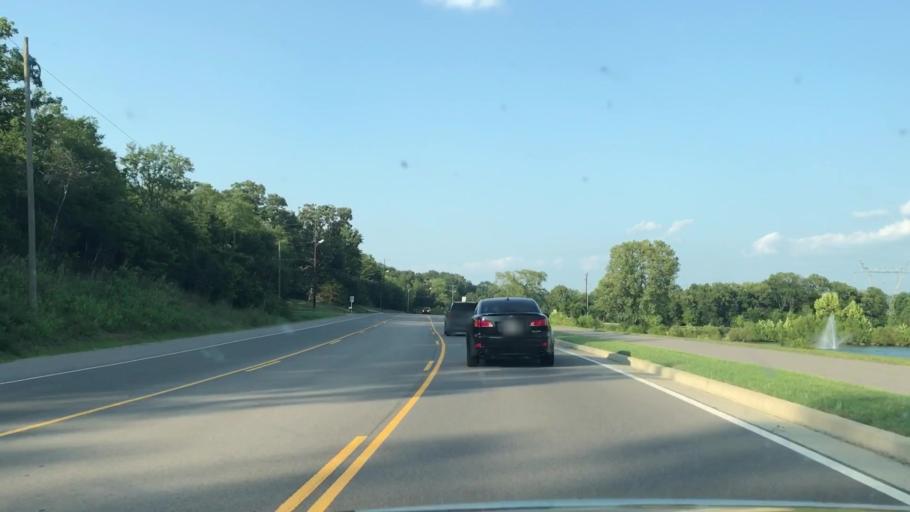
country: US
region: Tennessee
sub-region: Williamson County
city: Nolensville
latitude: 35.9897
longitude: -86.7032
